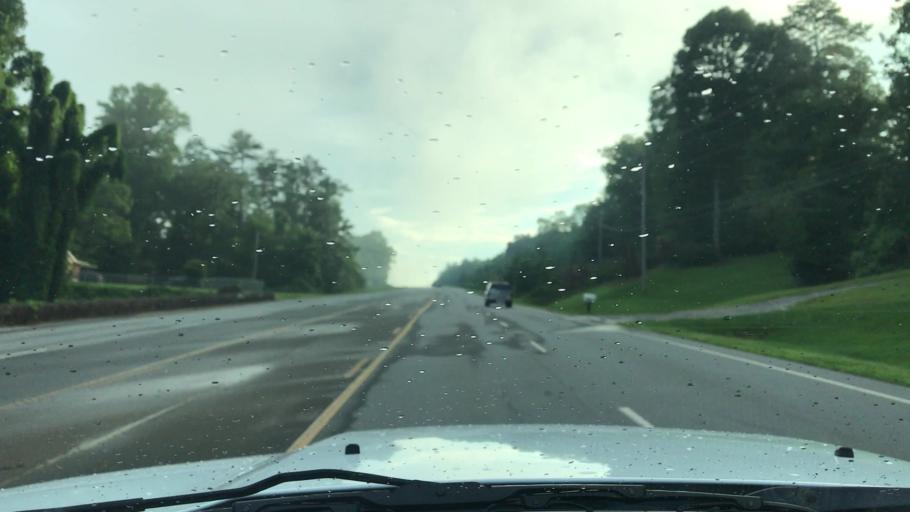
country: US
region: North Carolina
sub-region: Cherokee County
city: Murphy
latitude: 34.9993
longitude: -84.1462
